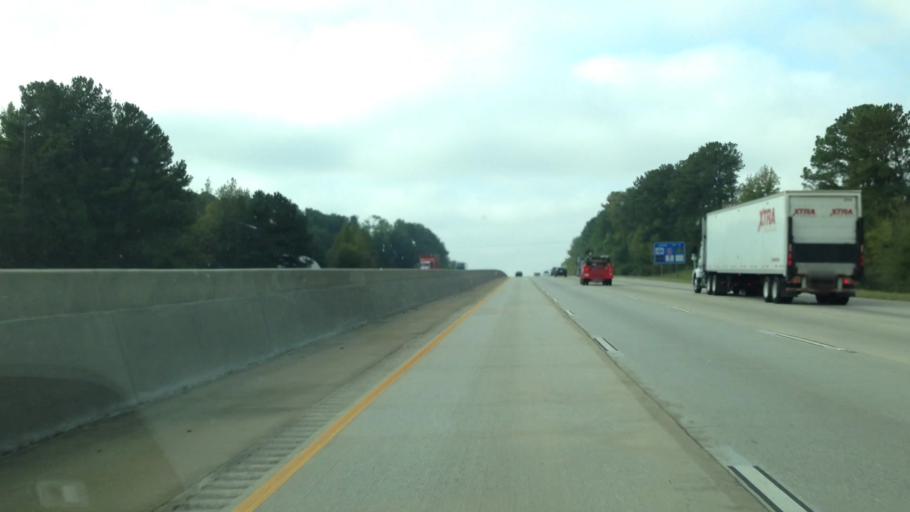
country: US
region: Georgia
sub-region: Coweta County
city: Newnan
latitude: 33.4218
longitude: -84.7279
